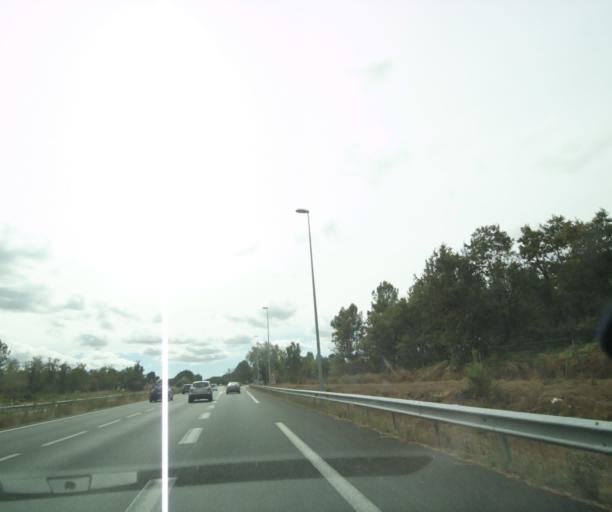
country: FR
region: Aquitaine
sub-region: Departement de la Gironde
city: Reignac
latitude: 45.1930
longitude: -0.4935
